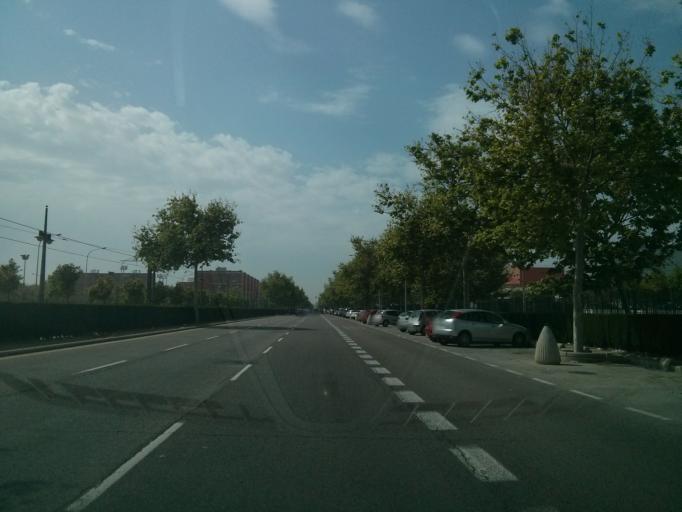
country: ES
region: Valencia
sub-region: Provincia de Valencia
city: Alboraya
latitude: 39.4772
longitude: -0.3356
